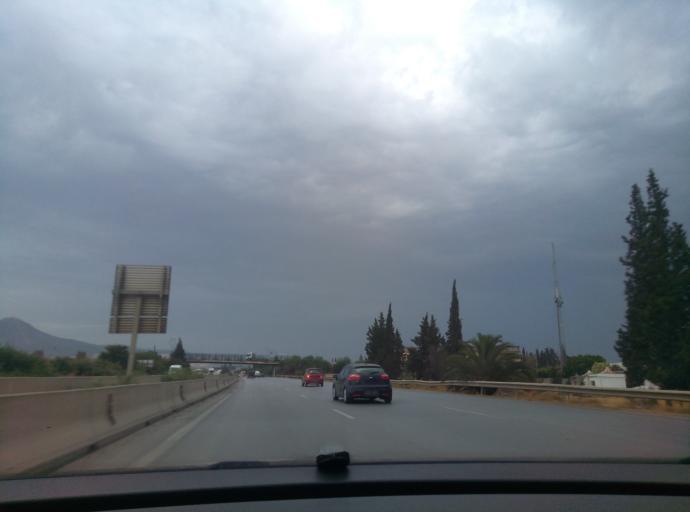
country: TN
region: Tunis
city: La Sebala du Mornag
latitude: 36.7183
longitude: 10.2669
